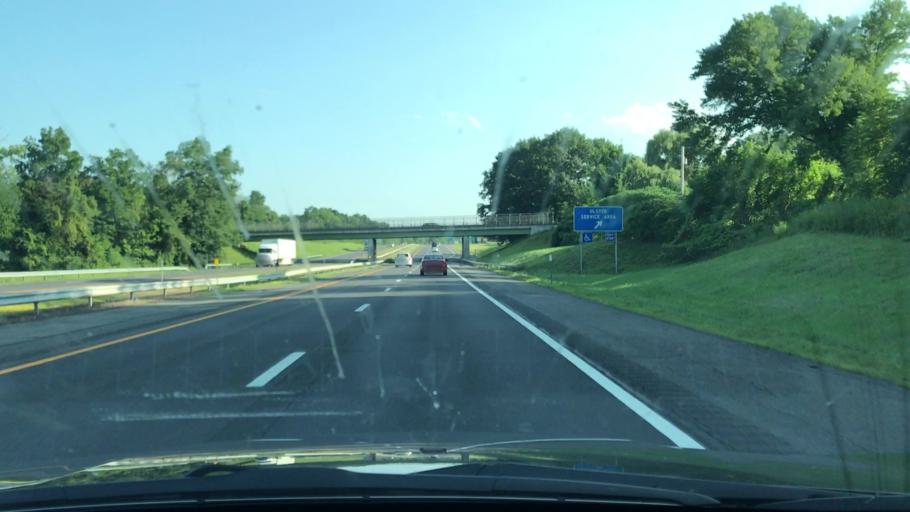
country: US
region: New York
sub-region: Ulster County
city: Lake Katrine
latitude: 42.0201
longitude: -73.9980
